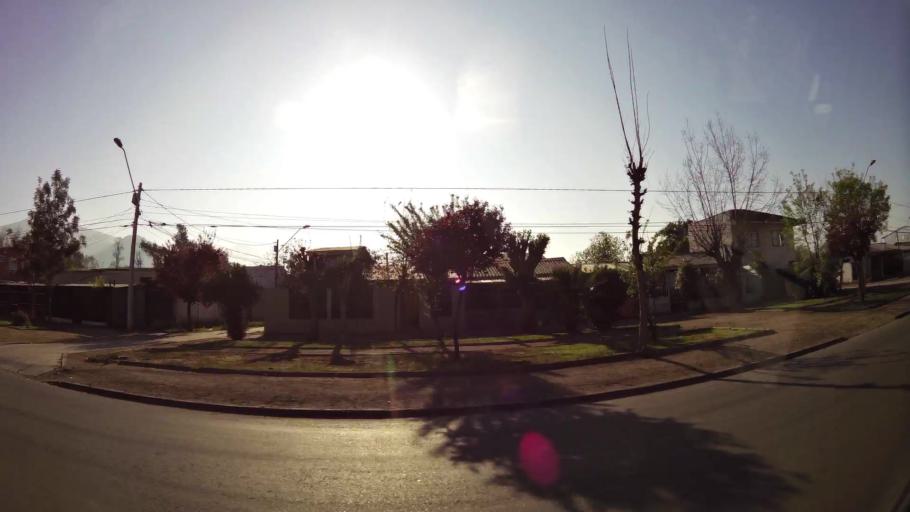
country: CL
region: Santiago Metropolitan
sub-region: Provincia de Santiago
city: Santiago
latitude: -33.3764
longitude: -70.6616
